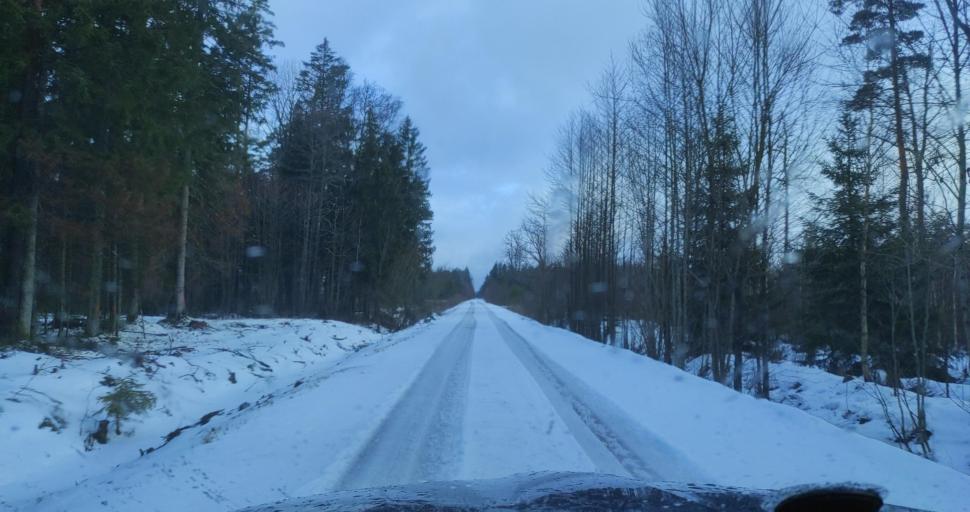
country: LV
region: Dundaga
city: Dundaga
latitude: 57.4079
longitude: 22.0891
